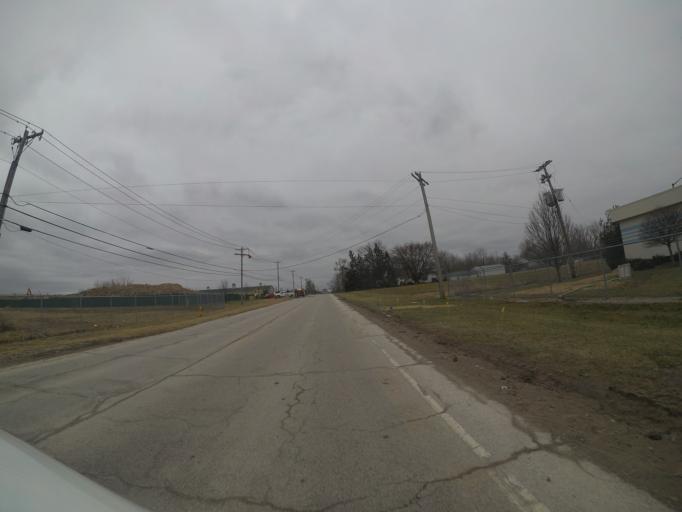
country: US
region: Ohio
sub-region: Wood County
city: Walbridge
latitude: 41.6140
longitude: -83.5125
